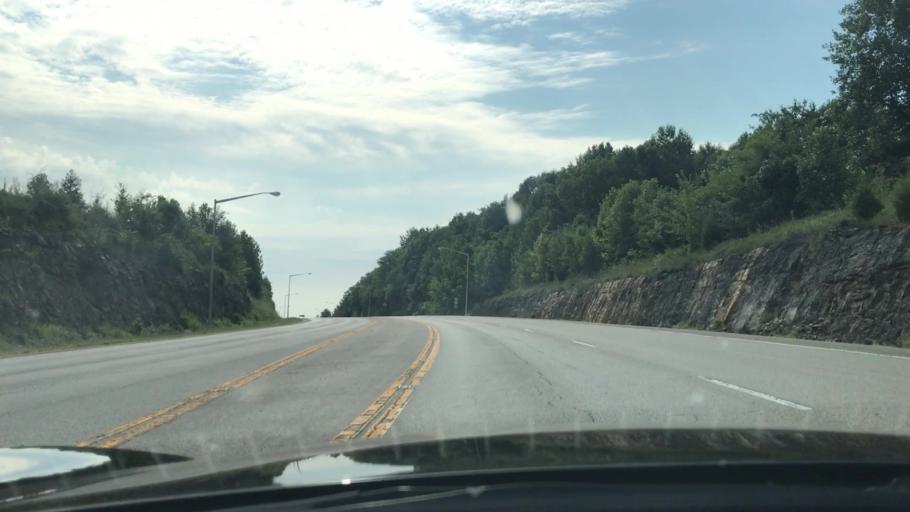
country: US
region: Kentucky
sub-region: Green County
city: Greensburg
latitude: 37.2735
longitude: -85.5071
